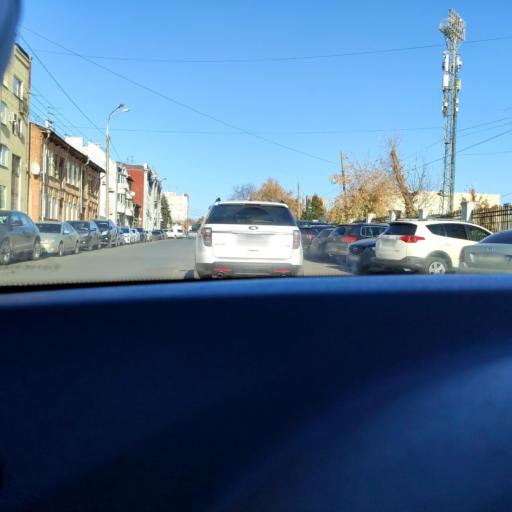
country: RU
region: Samara
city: Samara
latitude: 53.1875
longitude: 50.1068
